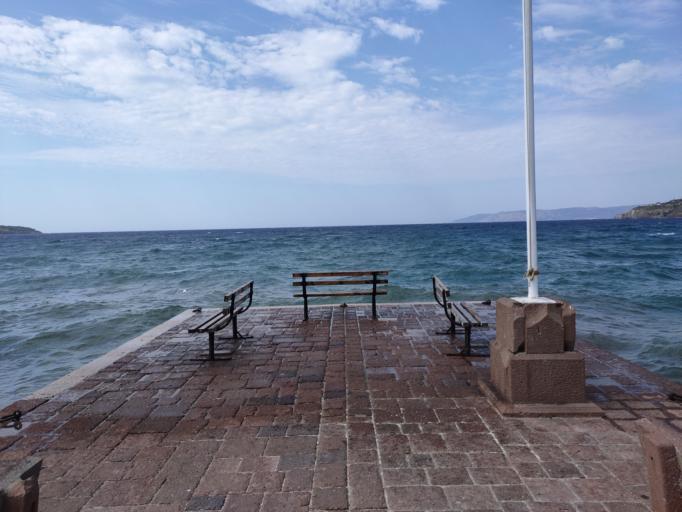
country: GR
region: North Aegean
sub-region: Nomos Lesvou
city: Petra
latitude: 39.3281
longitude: 26.1751
